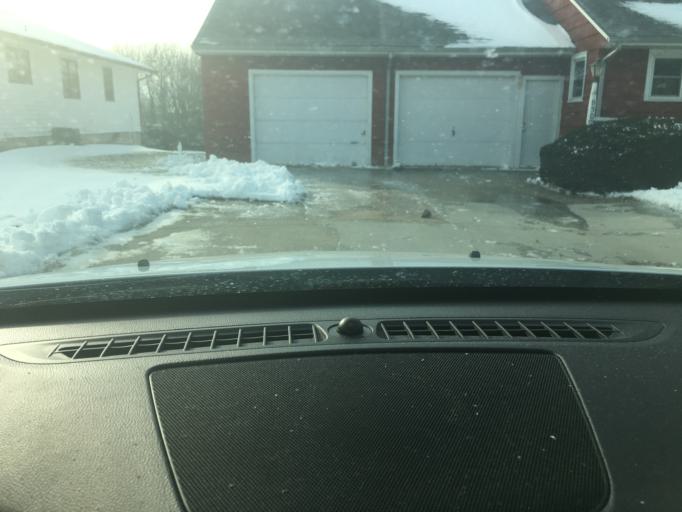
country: US
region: Illinois
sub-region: LaSalle County
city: Peru
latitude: 41.3327
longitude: -89.1166
